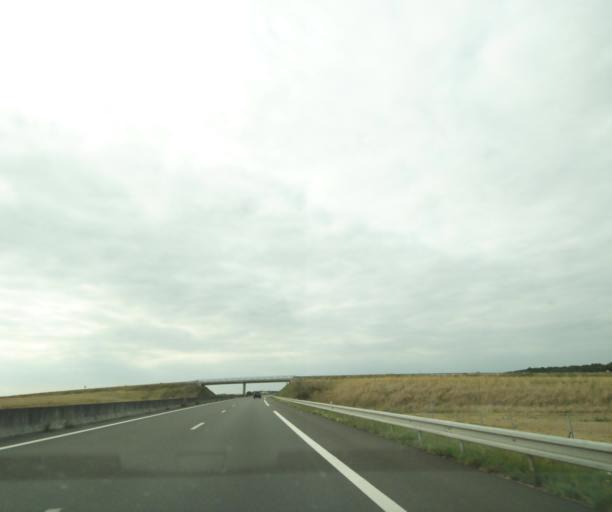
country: FR
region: Centre
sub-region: Departement d'Indre-et-Loire
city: Neuille-Pont-Pierre
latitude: 47.5981
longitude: 0.5400
